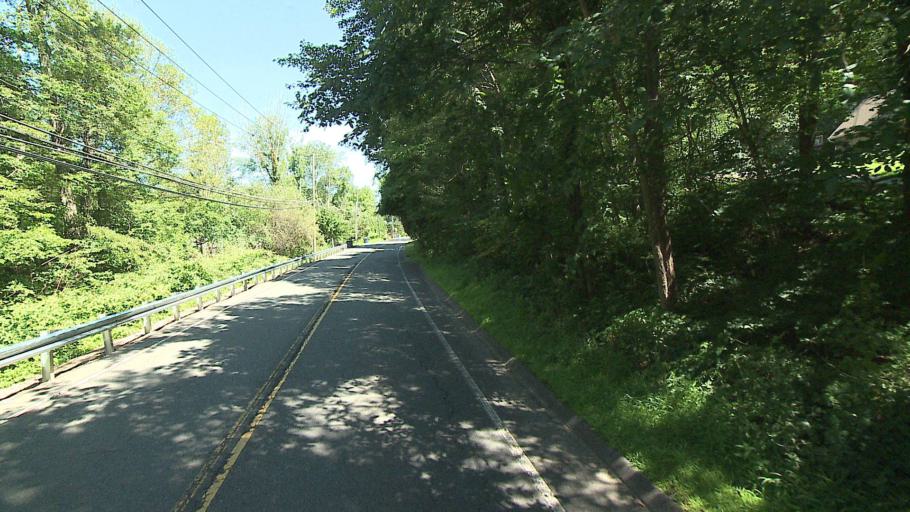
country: US
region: Connecticut
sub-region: Hartford County
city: Collinsville
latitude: 41.8418
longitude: -72.9257
